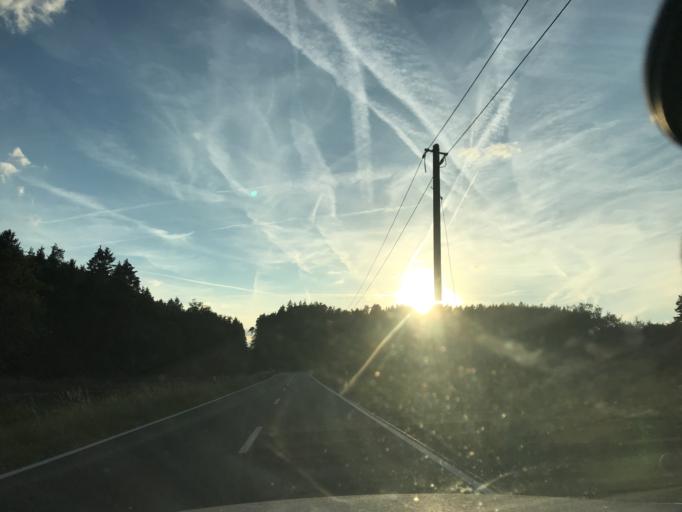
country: DE
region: Bavaria
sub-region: Upper Franconia
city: Pegnitz
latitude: 49.7319
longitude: 11.5563
